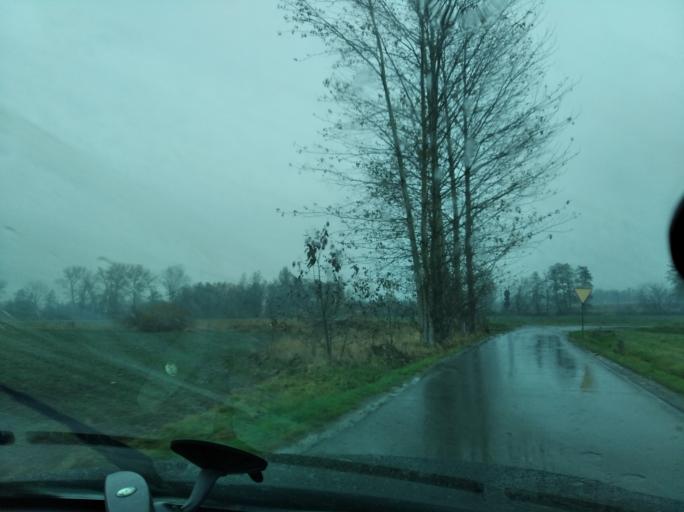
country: PL
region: Subcarpathian Voivodeship
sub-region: Powiat lancucki
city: Albigowa
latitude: 50.0373
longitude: 22.2178
